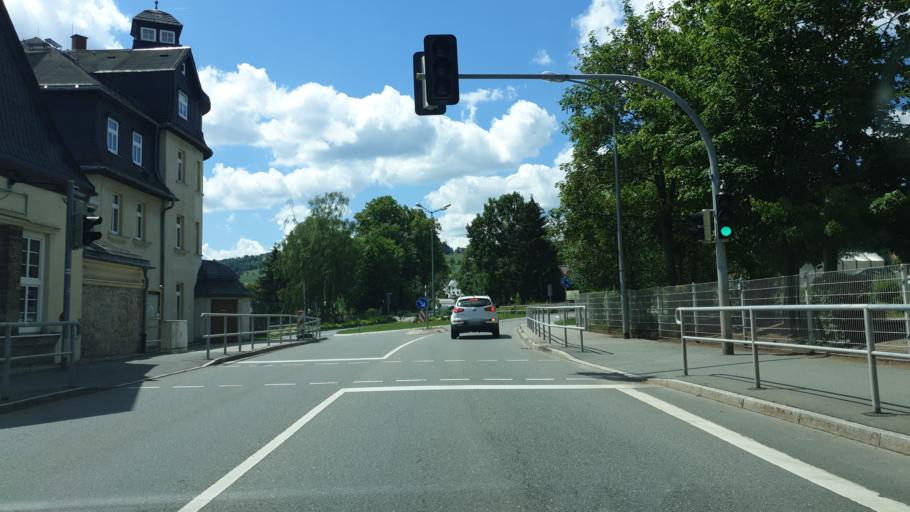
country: DE
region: Saxony
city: Schwarzenberg
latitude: 50.5342
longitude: 12.7722
